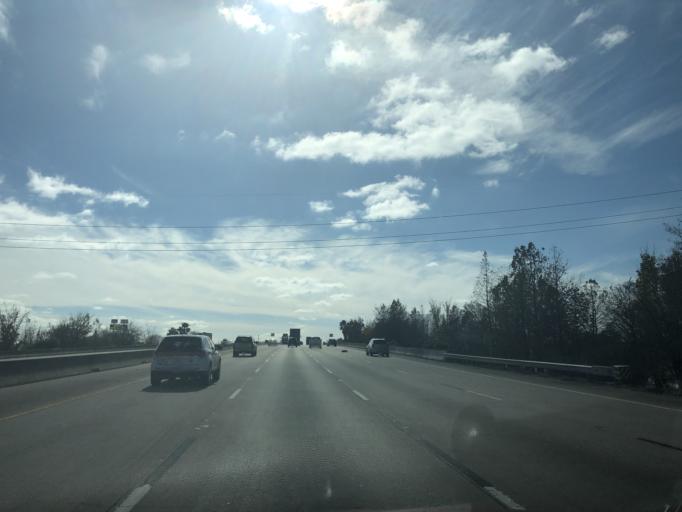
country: US
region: Texas
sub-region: Harris County
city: La Porte
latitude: 29.6764
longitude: -95.0298
